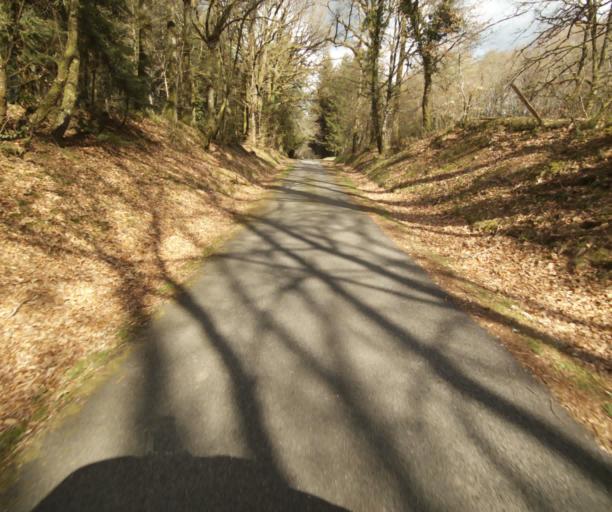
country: FR
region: Limousin
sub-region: Departement de la Correze
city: Argentat
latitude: 45.2268
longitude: 1.9299
